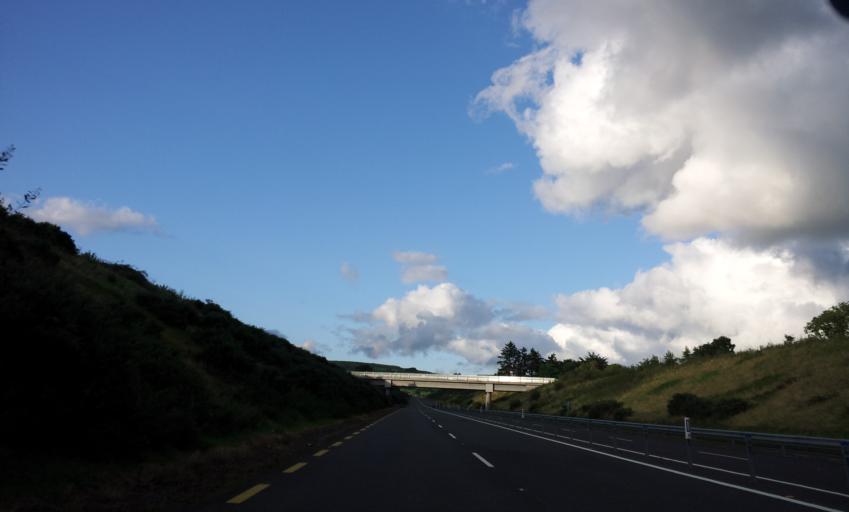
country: IE
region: Munster
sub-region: Ciarrai
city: Castleisland
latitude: 52.2485
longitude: -9.4805
